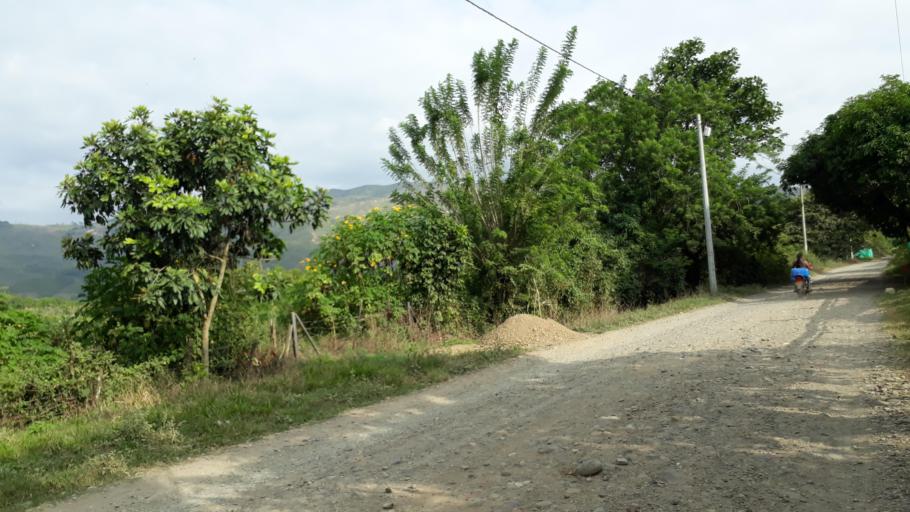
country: CO
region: Cauca
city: Buenos Aires
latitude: 3.1276
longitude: -76.6268
